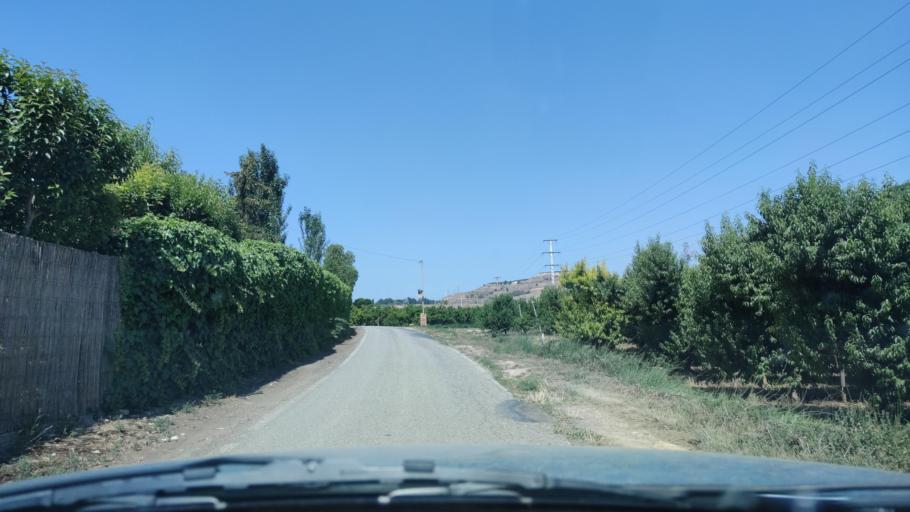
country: ES
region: Catalonia
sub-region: Provincia de Lleida
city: Torrefarrera
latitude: 41.6683
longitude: 0.5888
